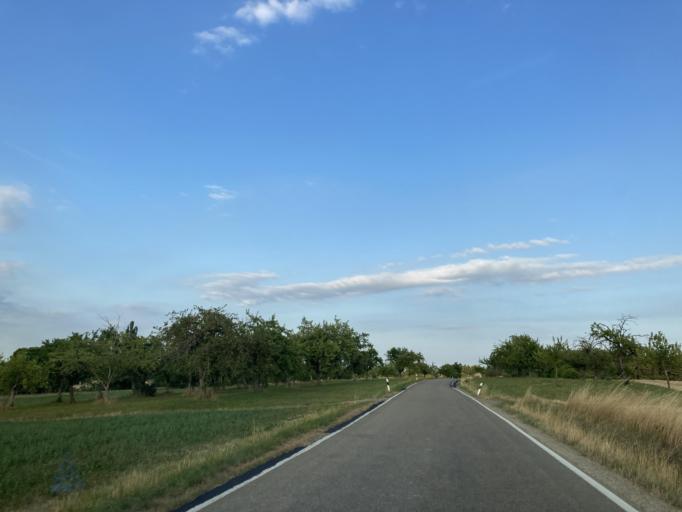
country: DE
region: Baden-Wuerttemberg
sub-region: Karlsruhe Region
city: Ebhausen
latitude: 48.6198
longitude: 8.6616
